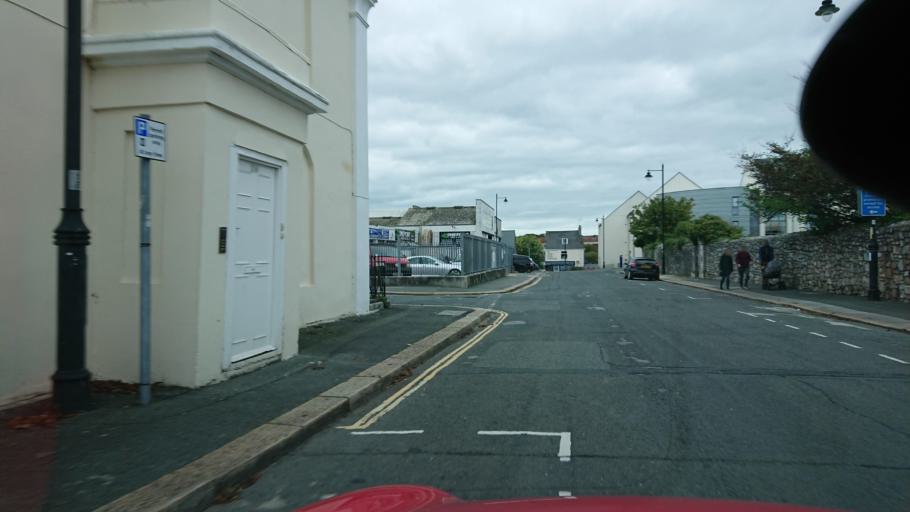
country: GB
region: England
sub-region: Plymouth
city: Plymouth
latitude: 50.3678
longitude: -4.1583
